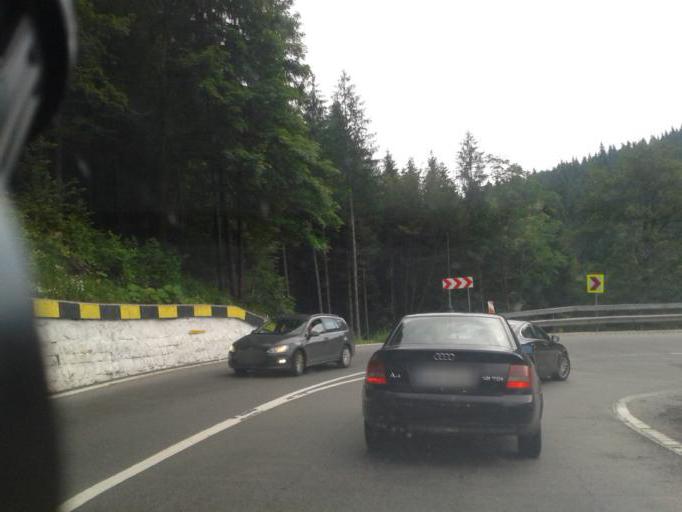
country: RO
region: Brasov
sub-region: Oras Predeal
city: Predeal
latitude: 45.5184
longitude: 25.5753
